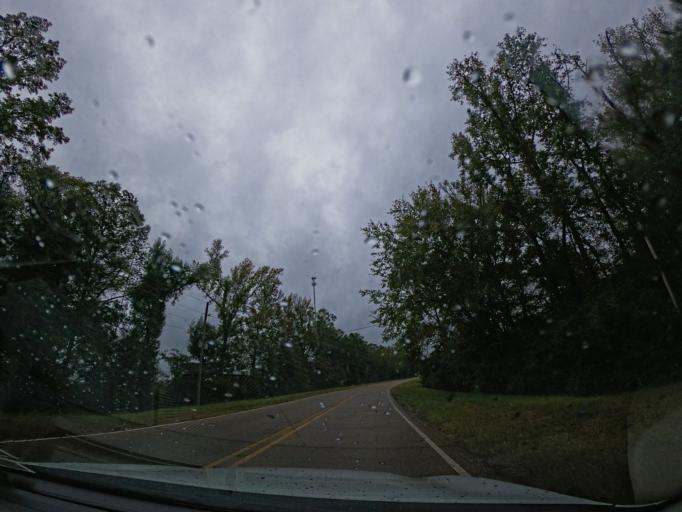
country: US
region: Louisiana
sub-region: Bienville Parish
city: Arcadia
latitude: 32.5529
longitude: -93.0532
